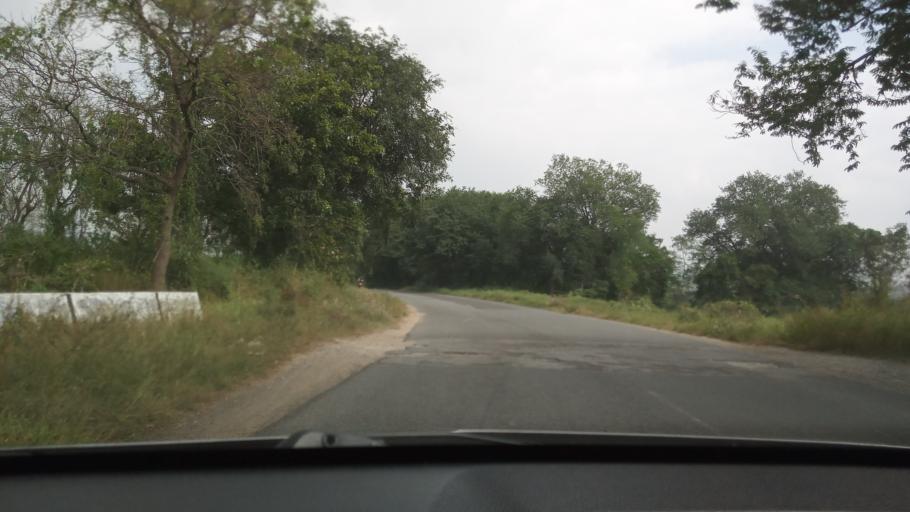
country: IN
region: Andhra Pradesh
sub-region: Chittoor
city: Madanapalle
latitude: 13.6517
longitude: 78.8289
